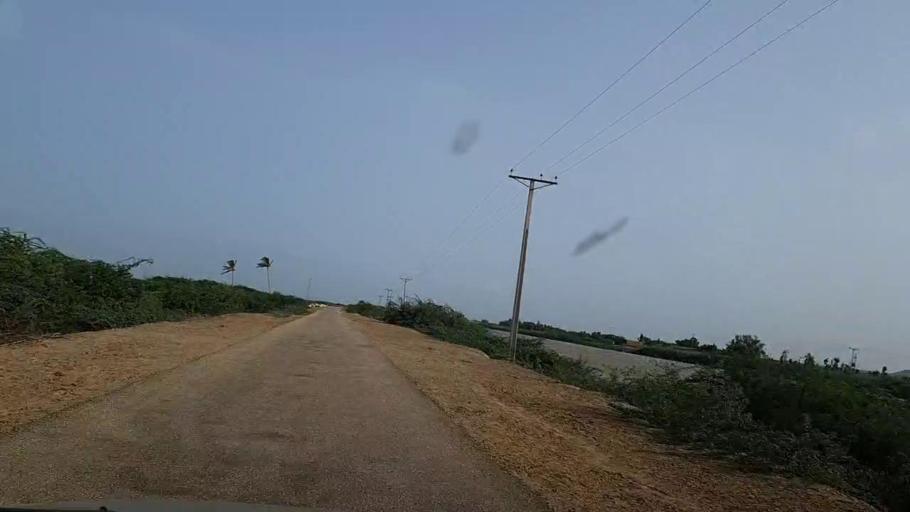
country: PK
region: Sindh
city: Kotri
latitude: 25.1929
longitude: 68.2585
